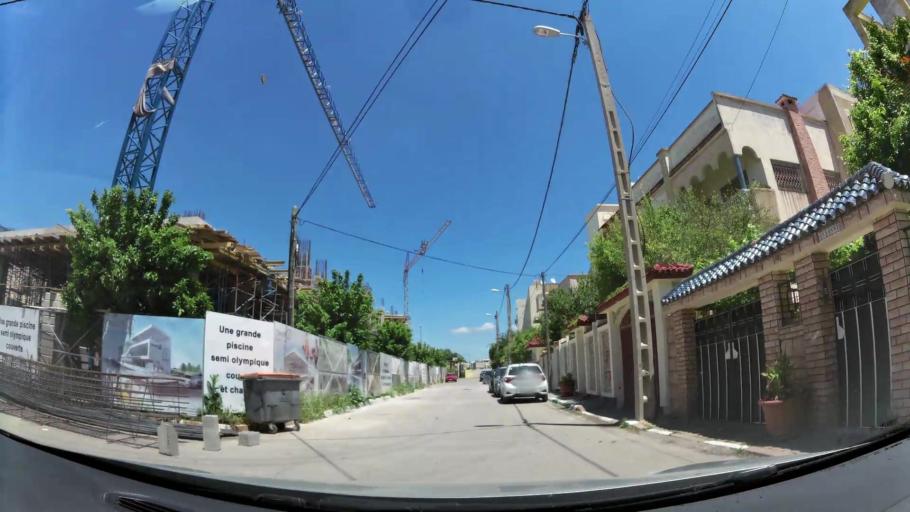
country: MA
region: Fes-Boulemane
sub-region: Fes
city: Fes
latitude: 34.0228
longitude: -5.0156
